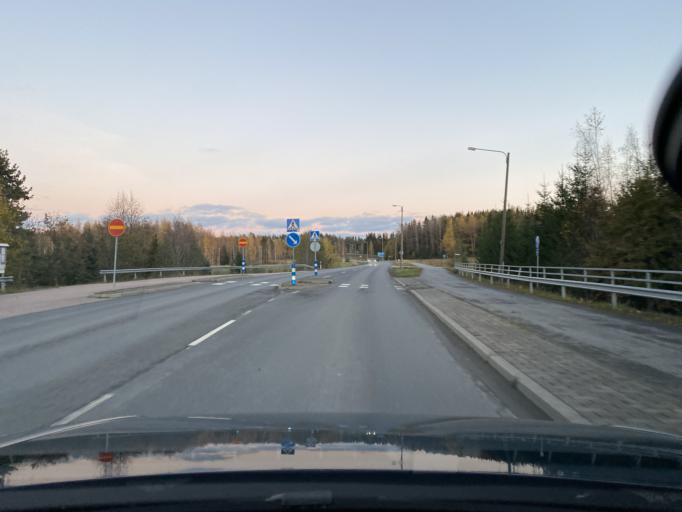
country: FI
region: Pirkanmaa
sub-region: Tampere
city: Lempaeaelae
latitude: 61.3281
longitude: 23.7664
